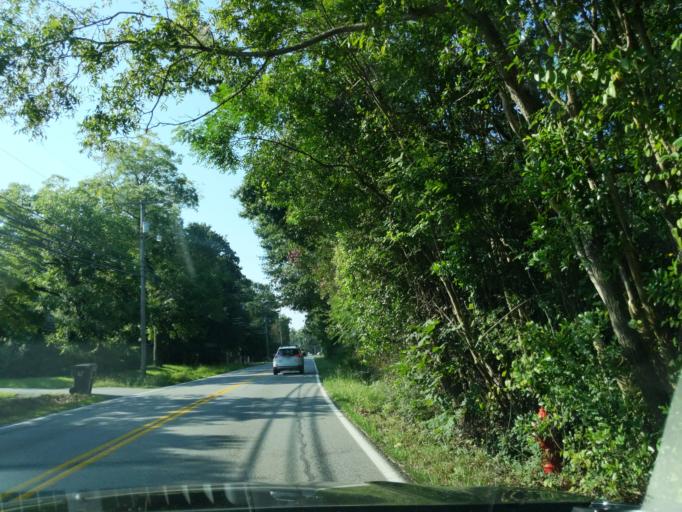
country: US
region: South Carolina
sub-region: Newberry County
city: Prosperity
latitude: 34.2056
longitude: -81.5317
